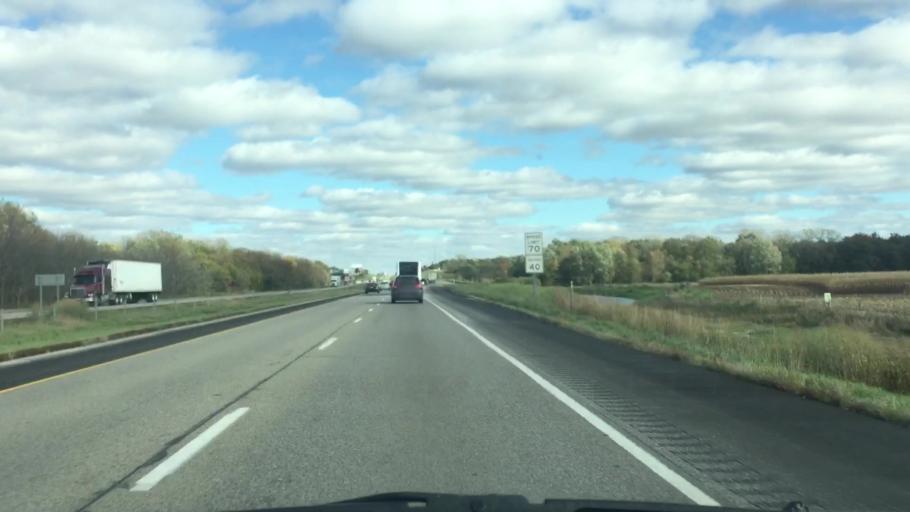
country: US
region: Iowa
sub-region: Cedar County
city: Tipton
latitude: 41.6457
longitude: -91.1429
